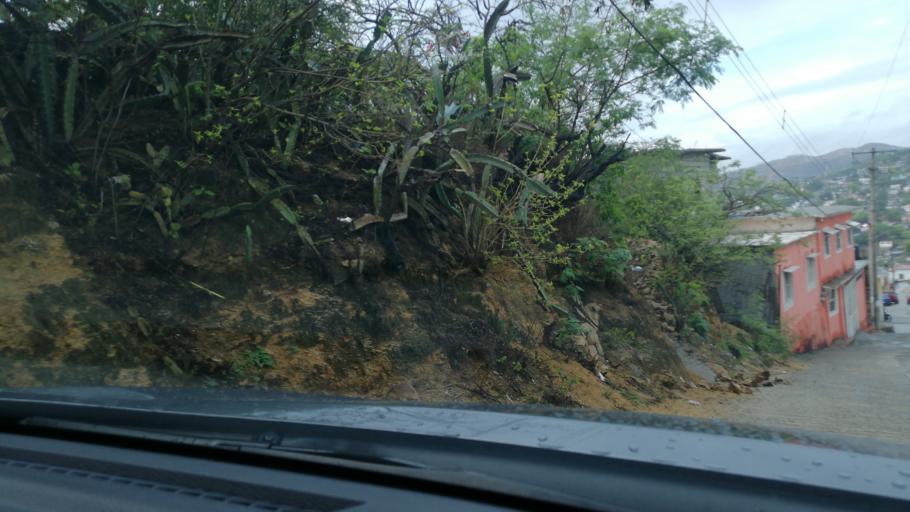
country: MX
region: Oaxaca
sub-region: Salina Cruz
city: Salina Cruz
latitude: 16.1882
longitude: -95.1962
